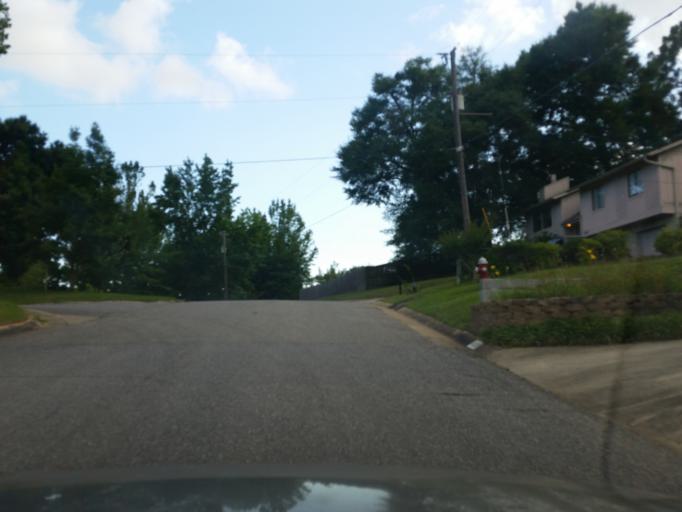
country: US
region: Florida
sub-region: Escambia County
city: Ferry Pass
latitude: 30.5117
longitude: -87.1744
